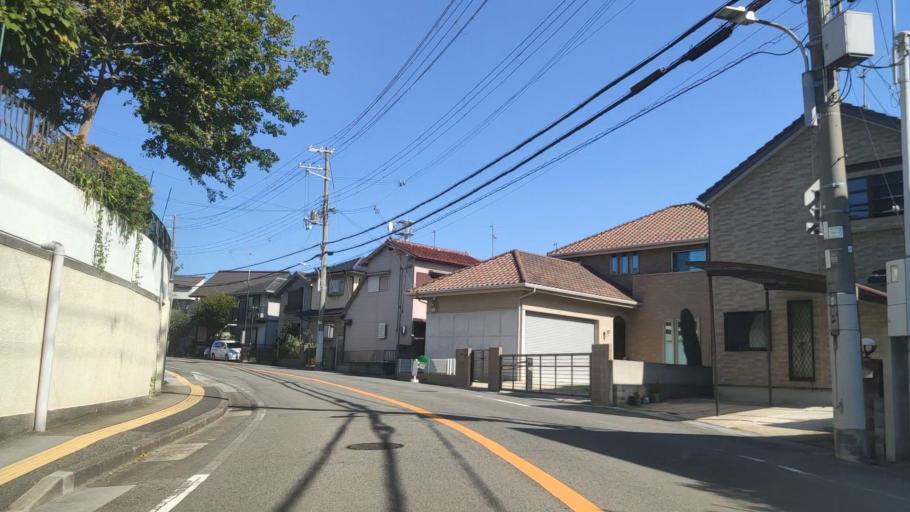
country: JP
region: Hyogo
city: Akashi
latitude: 34.6522
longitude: 135.0032
